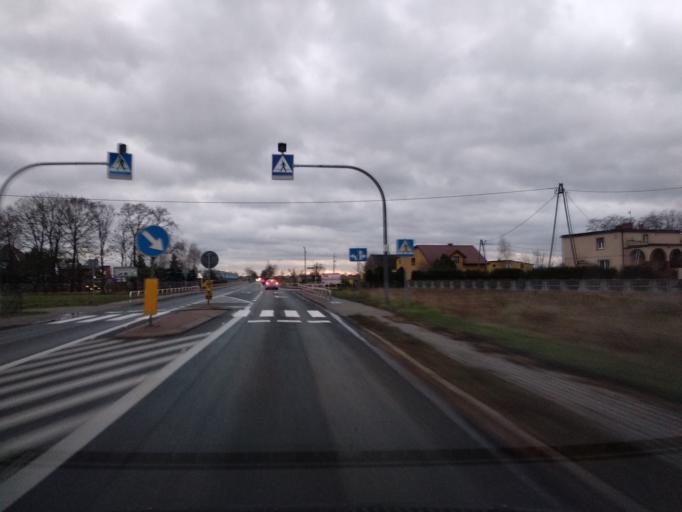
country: PL
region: Greater Poland Voivodeship
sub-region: Powiat koninski
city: Rychwal
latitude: 52.0960
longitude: 18.1666
